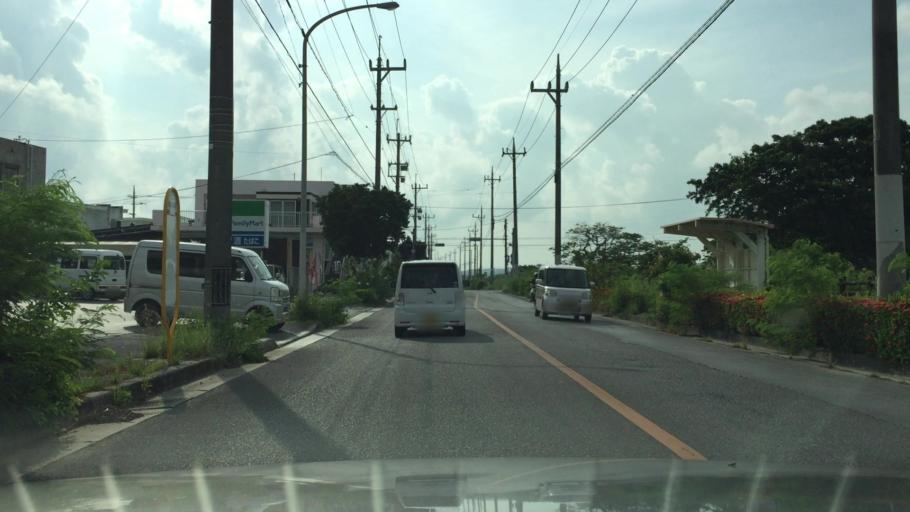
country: JP
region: Okinawa
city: Ishigaki
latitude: 24.3490
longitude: 124.1651
